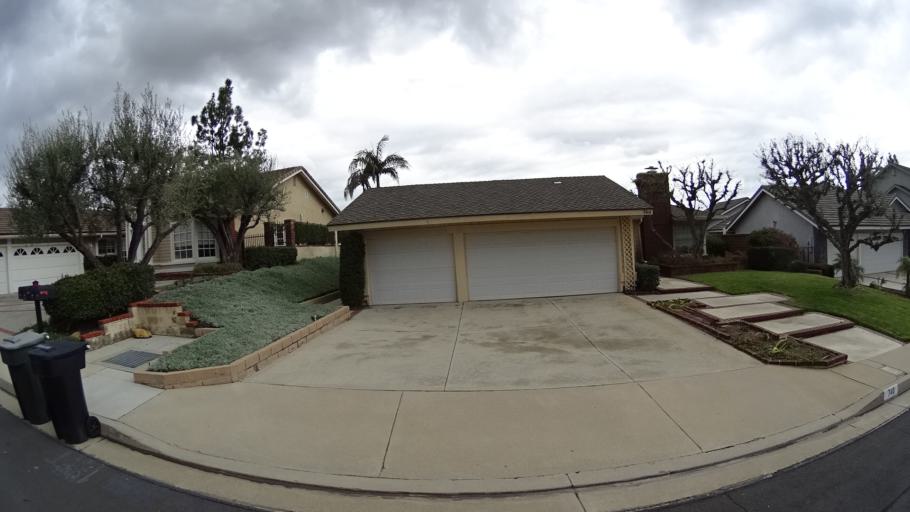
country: US
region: California
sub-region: Orange County
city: Villa Park
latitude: 33.8448
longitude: -117.7514
